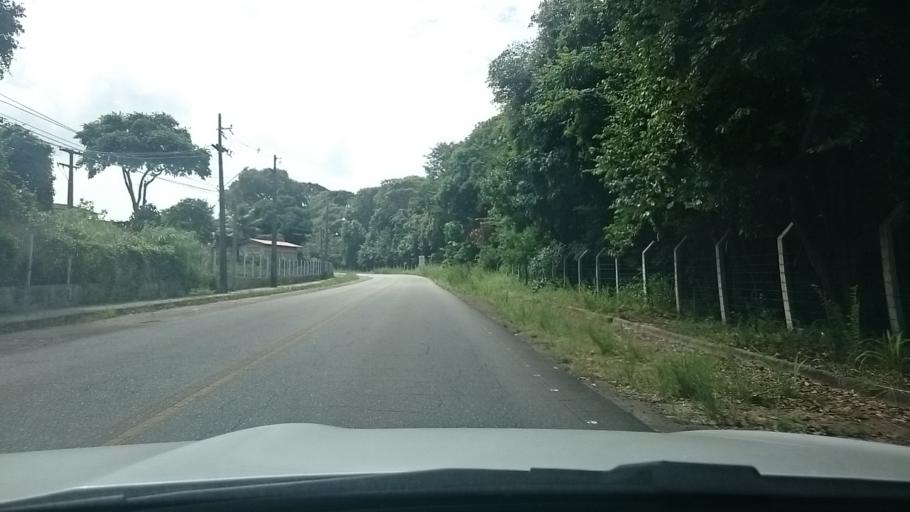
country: BR
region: Paraiba
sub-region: Joao Pessoa
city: Joao Pessoa
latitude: -7.1422
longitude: -34.8468
